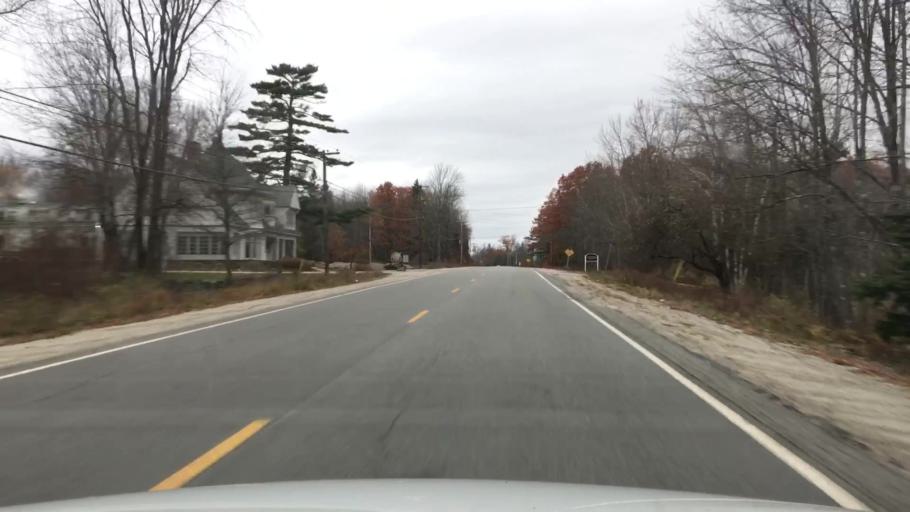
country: US
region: Maine
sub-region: Hancock County
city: Sedgwick
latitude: 44.4004
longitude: -68.5900
